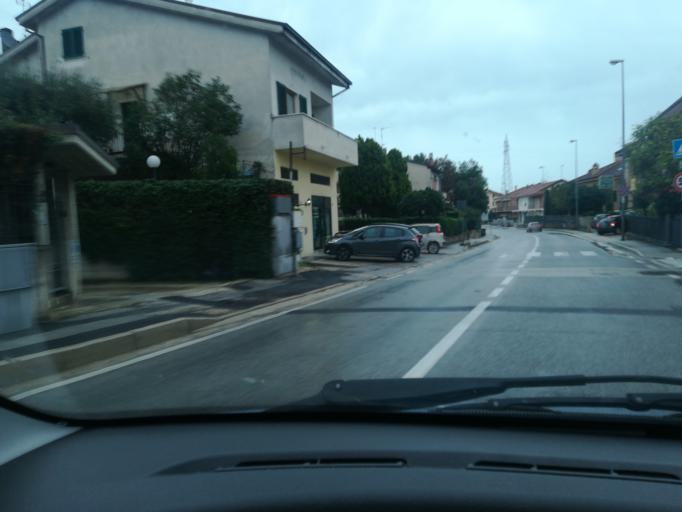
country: IT
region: The Marches
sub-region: Provincia di Macerata
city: Santa Maria Apparente
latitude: 43.2971
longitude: 13.6934
